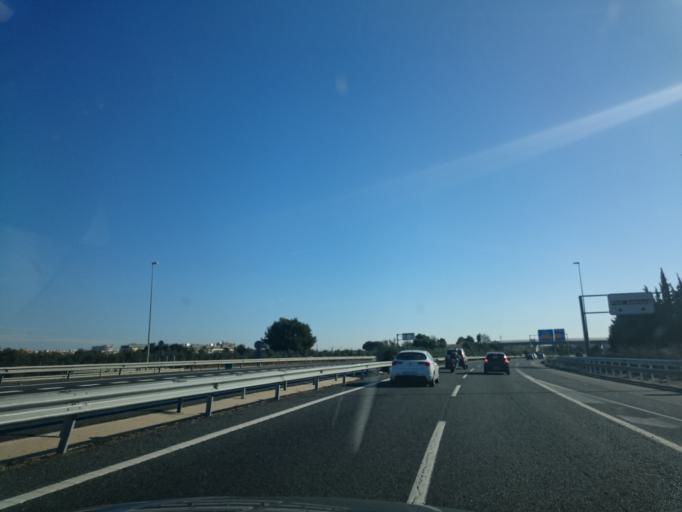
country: ES
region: Catalonia
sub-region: Provincia de Tarragona
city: Vila-seca
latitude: 41.1047
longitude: 1.1366
